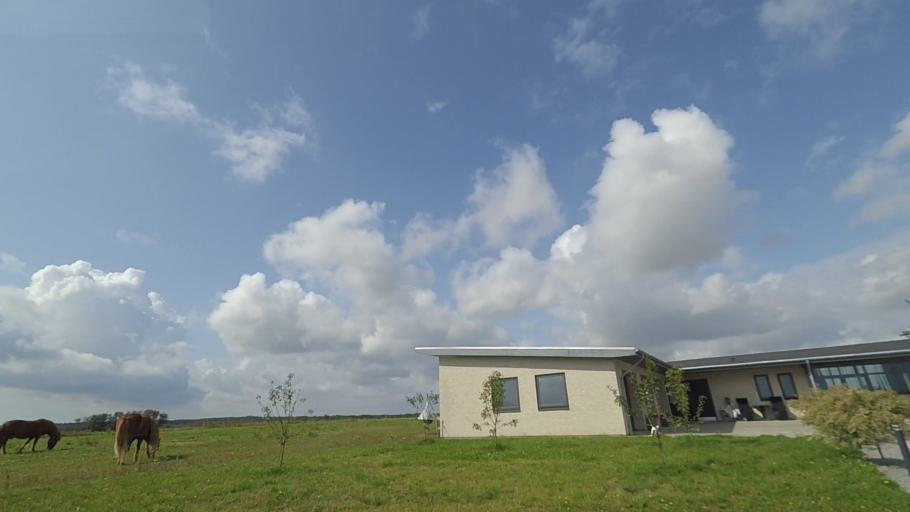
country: DK
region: Central Jutland
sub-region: Syddjurs Kommune
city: Ryomgard
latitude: 56.4747
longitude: 10.5071
